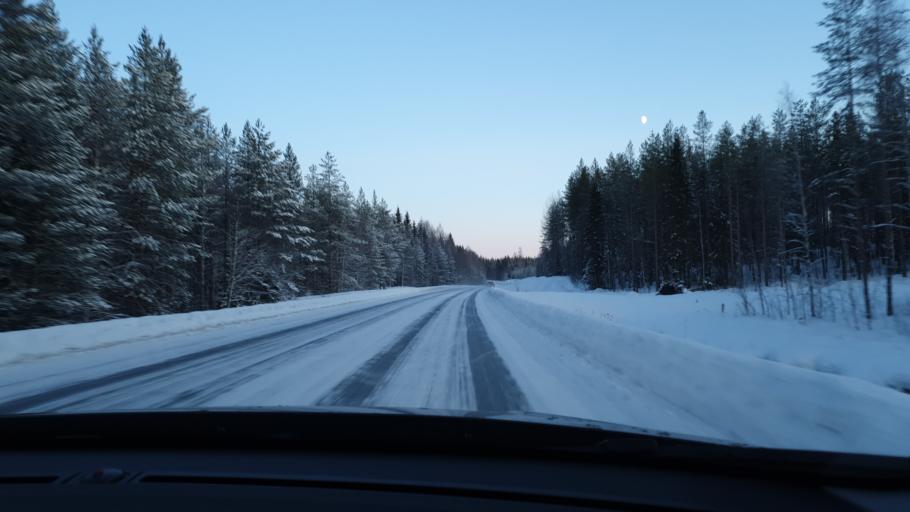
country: FI
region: North Karelia
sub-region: Pielisen Karjala
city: Valtimo
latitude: 64.0844
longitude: 28.9306
